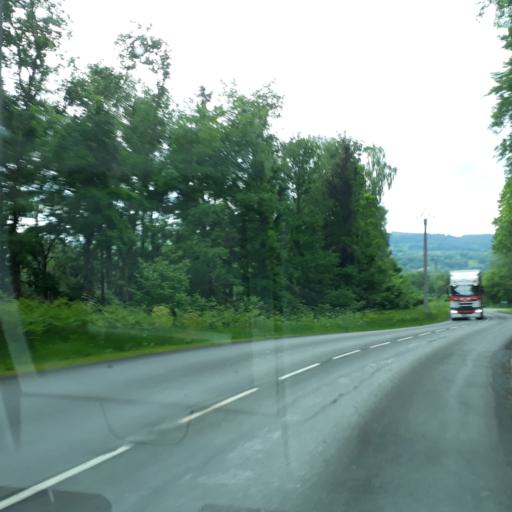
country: FR
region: Limousin
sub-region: Departement de la Haute-Vienne
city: Eymoutiers
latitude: 45.7531
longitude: 1.7437
